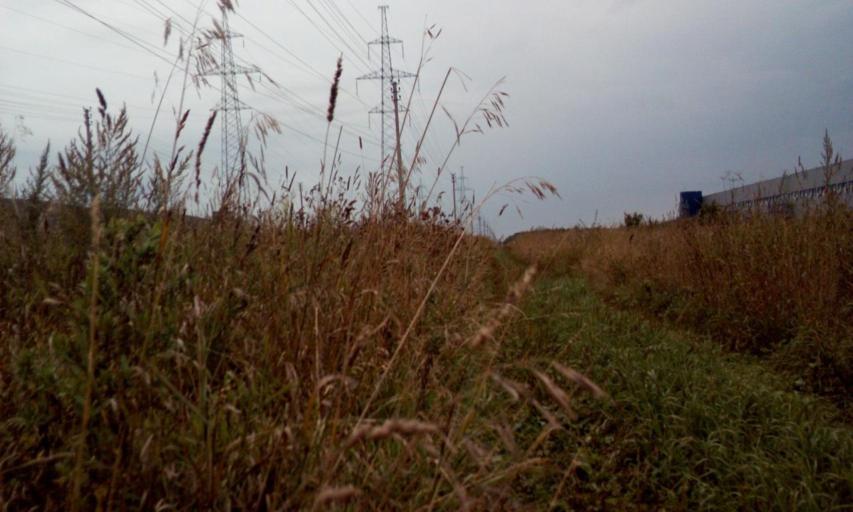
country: RU
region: Moskovskaya
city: Aprelevka
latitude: 55.5819
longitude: 37.1055
